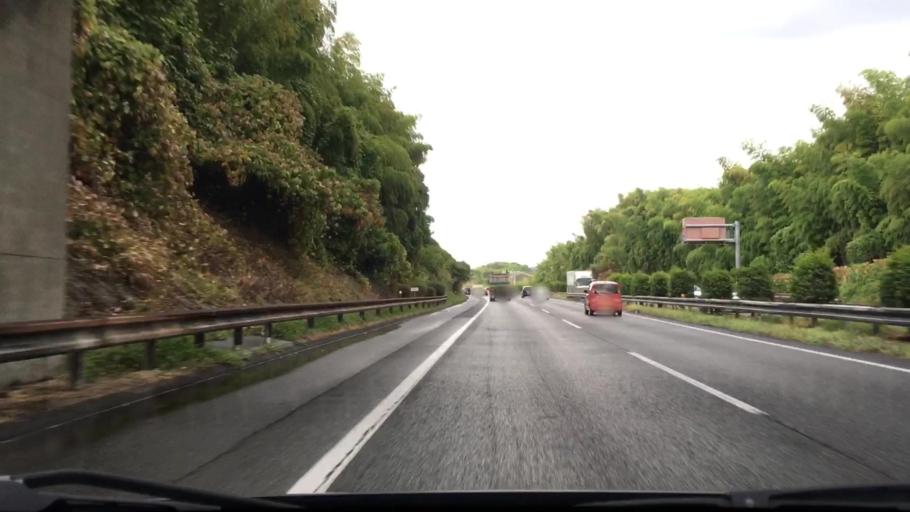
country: JP
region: Fukuoka
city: Koga
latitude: 33.7220
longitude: 130.4980
